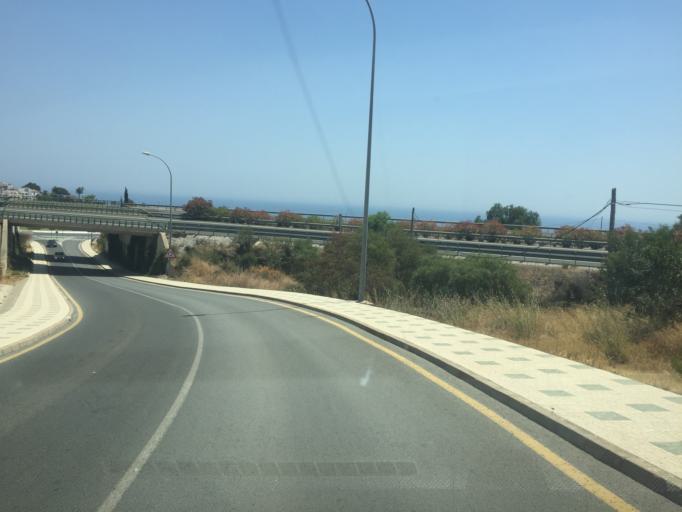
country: ES
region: Andalusia
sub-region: Provincia de Malaga
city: Nerja
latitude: 36.7605
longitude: -3.8483
